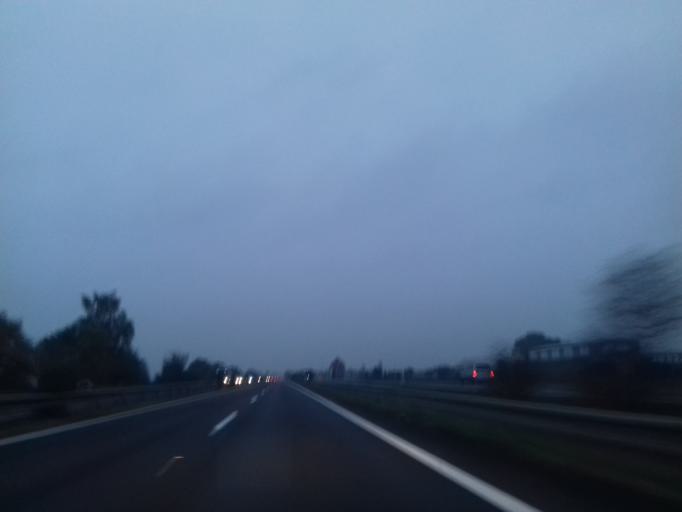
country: CZ
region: Olomoucky
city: Naklo
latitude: 49.6543
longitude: 17.1176
